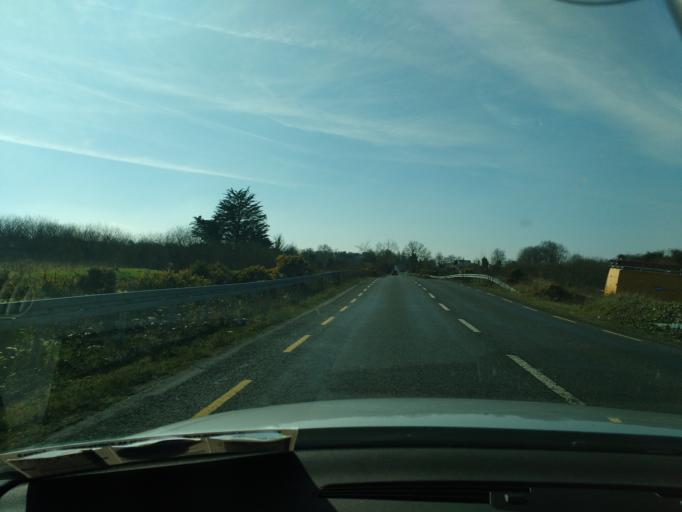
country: IE
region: Munster
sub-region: County Limerick
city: Castleconnell
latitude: 52.6911
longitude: -8.4757
